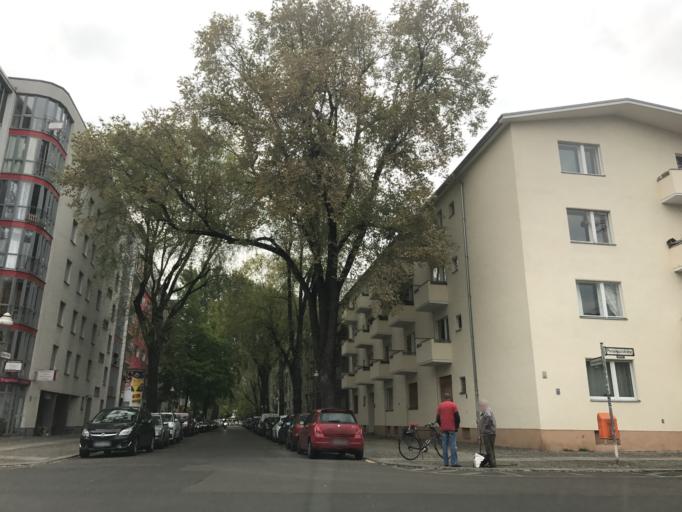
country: DE
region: Berlin
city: Halensee
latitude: 52.5077
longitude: 13.3005
